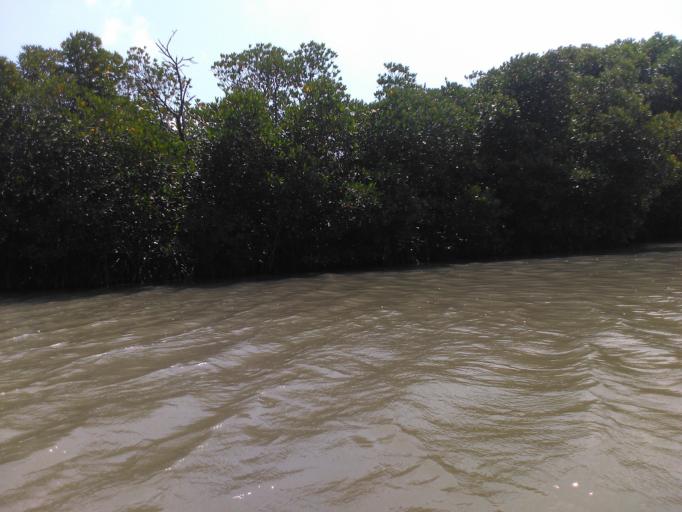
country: IN
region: Tamil Nadu
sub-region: Cuddalore
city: Annamalainagar
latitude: 11.4400
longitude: 79.7873
